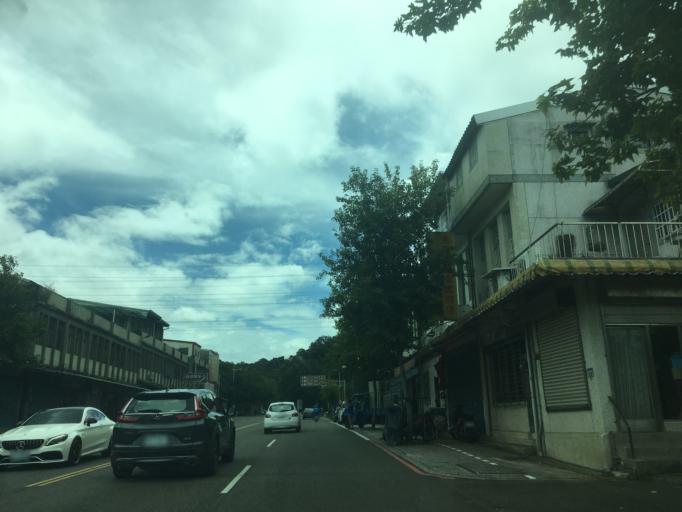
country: TW
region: Taiwan
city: Daxi
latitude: 24.8409
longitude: 121.2902
